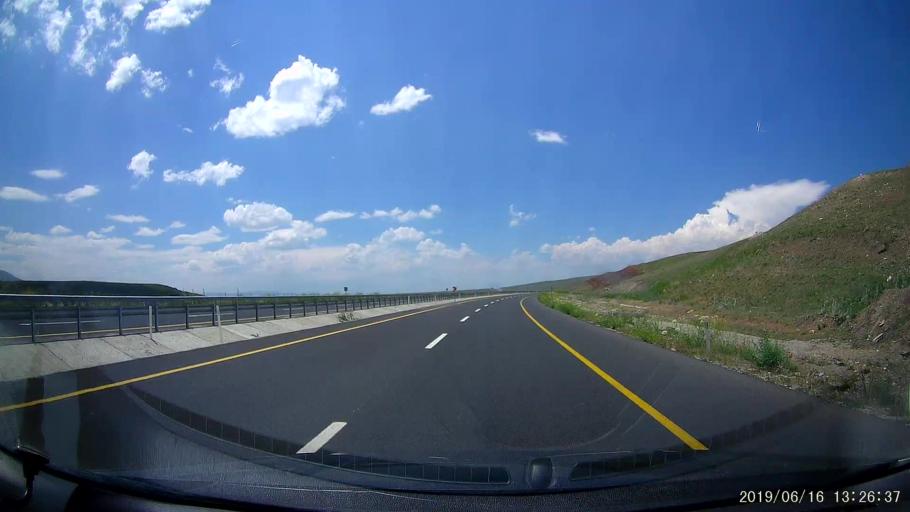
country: TR
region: Agri
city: Taslicay
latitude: 39.6601
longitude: 43.3237
